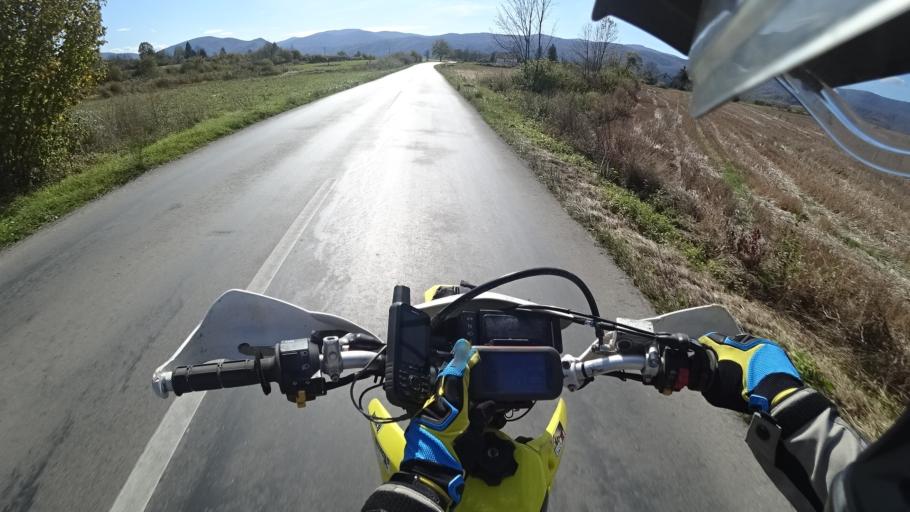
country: HR
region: Karlovacka
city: Plaski
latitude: 45.1044
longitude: 15.3592
